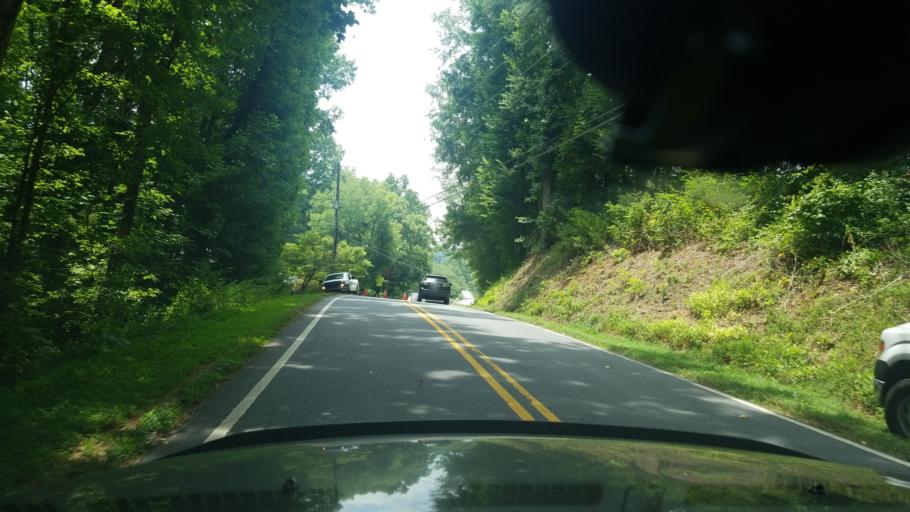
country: US
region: Georgia
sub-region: Forsyth County
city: Cumming
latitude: 34.1936
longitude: -84.2222
